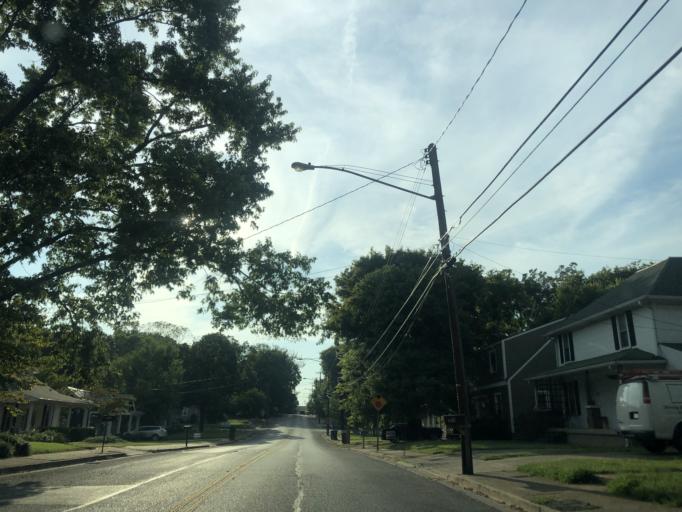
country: US
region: Tennessee
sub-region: Davidson County
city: Oak Hill
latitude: 36.1202
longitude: -86.7441
